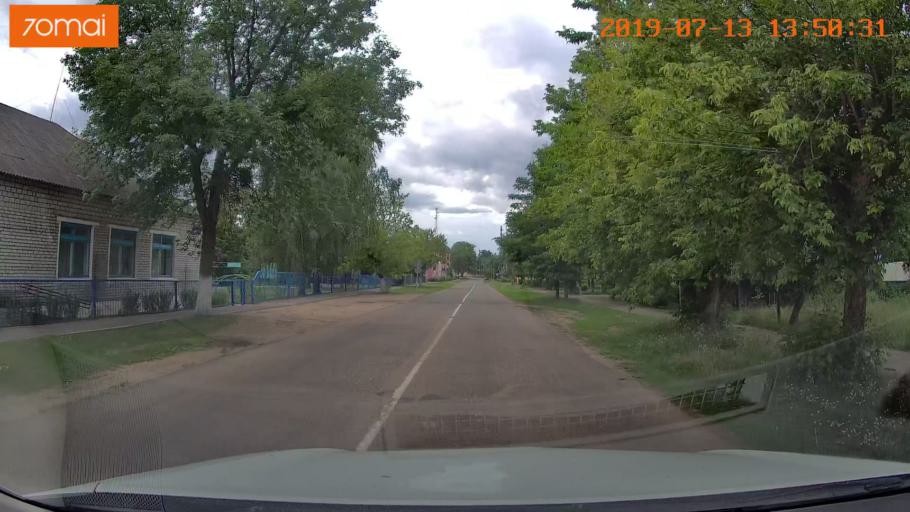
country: BY
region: Mogilev
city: Asipovichy
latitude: 53.2973
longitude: 28.6409
